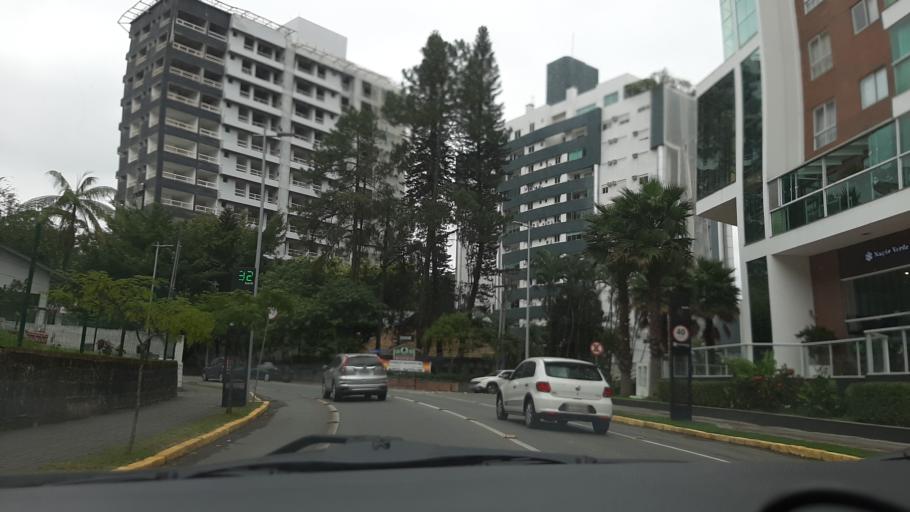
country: BR
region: Santa Catarina
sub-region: Joinville
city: Joinville
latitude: -26.3069
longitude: -48.8550
